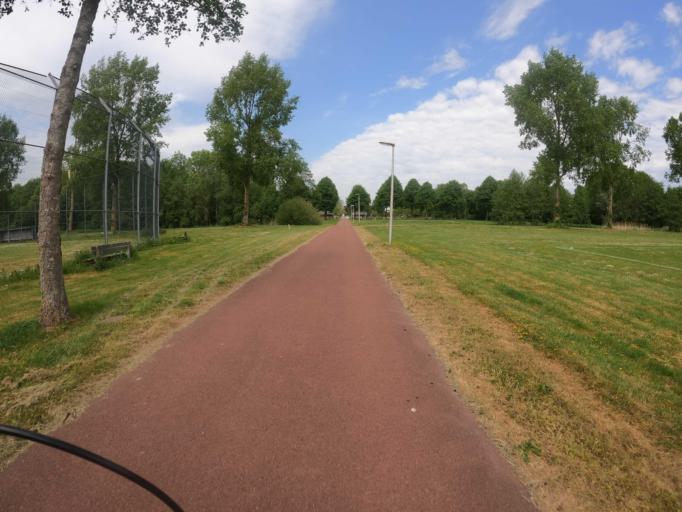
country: NL
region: Flevoland
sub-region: Gemeente Zeewolde
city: Zeewolde
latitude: 52.3271
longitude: 5.5189
